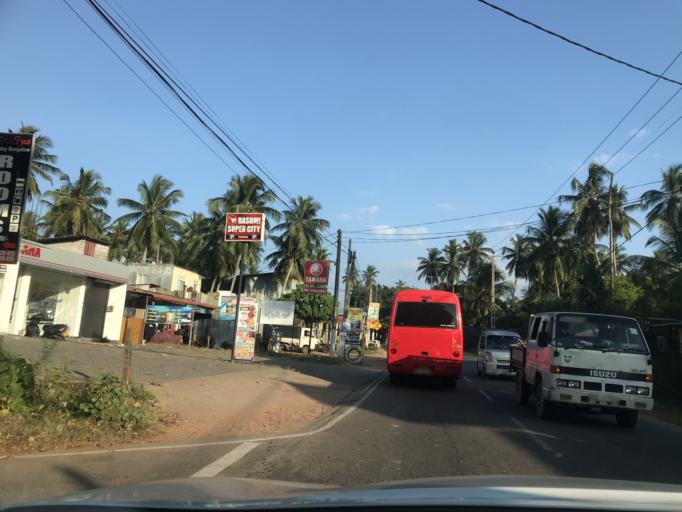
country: LK
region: Western
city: Ja Ela
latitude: 7.1013
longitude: 79.9133
